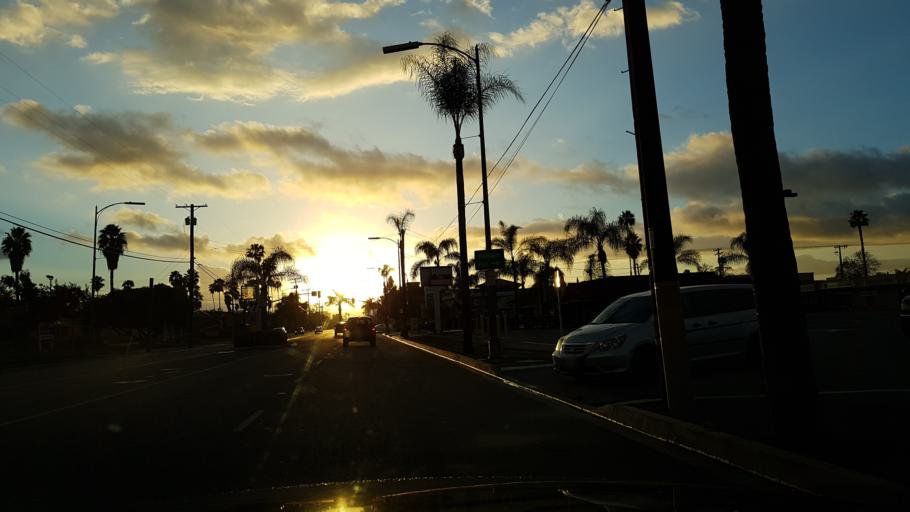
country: US
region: California
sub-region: San Diego County
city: Escondido
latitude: 33.1346
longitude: -117.0583
